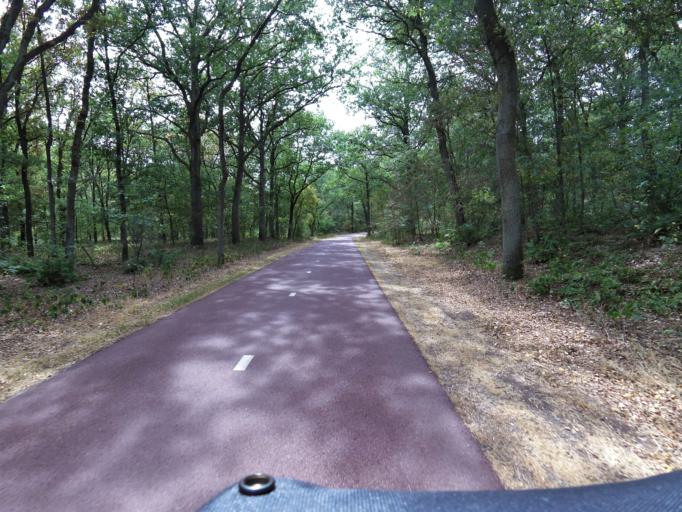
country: NL
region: Limburg
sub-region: Gemeente Venlo
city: Arcen
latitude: 51.5102
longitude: 6.1786
